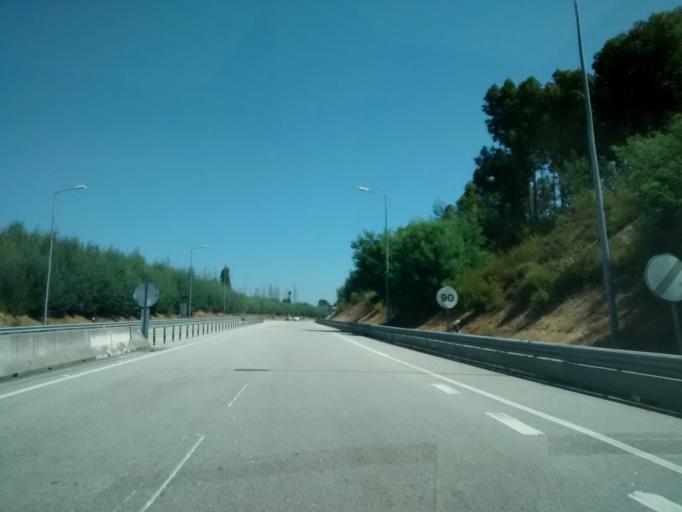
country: PT
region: Coimbra
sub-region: Tabua
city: Tabua
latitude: 40.3698
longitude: -8.0402
